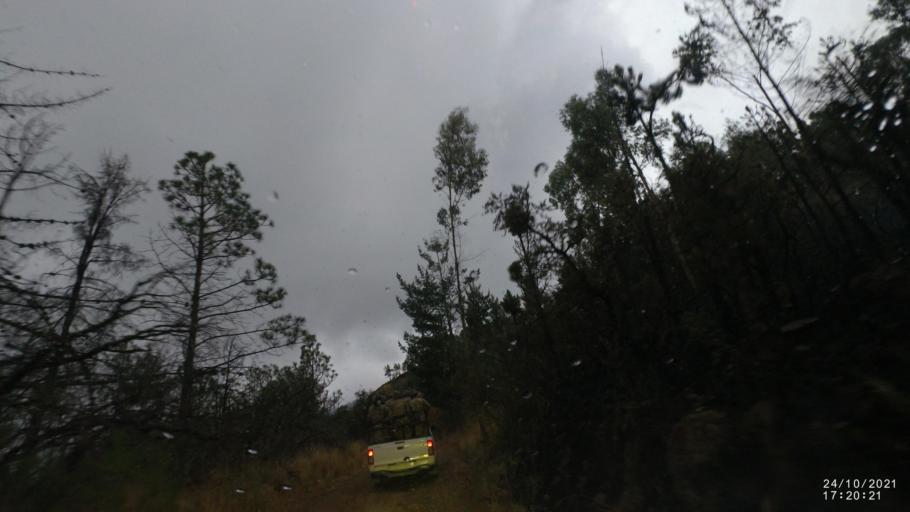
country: BO
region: Cochabamba
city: Cochabamba
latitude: -17.3283
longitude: -66.1358
